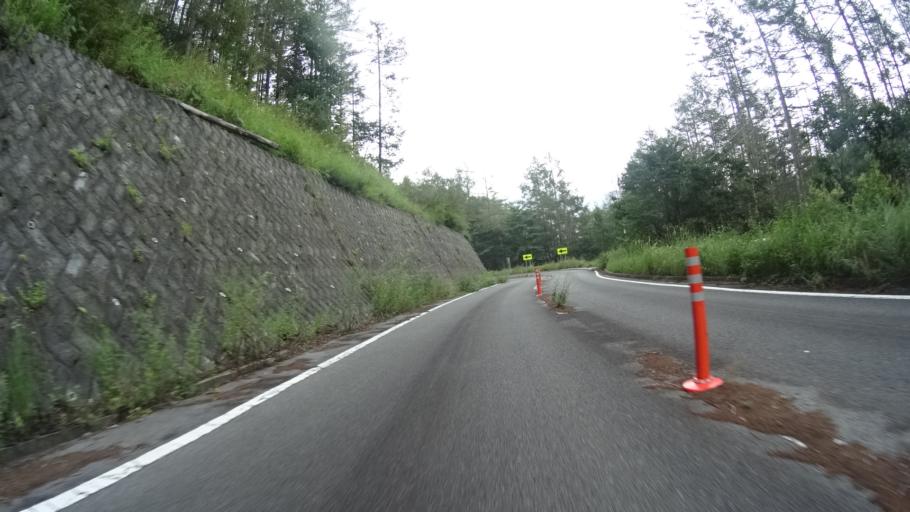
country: JP
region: Yamanashi
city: Enzan
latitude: 35.7990
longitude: 138.6500
